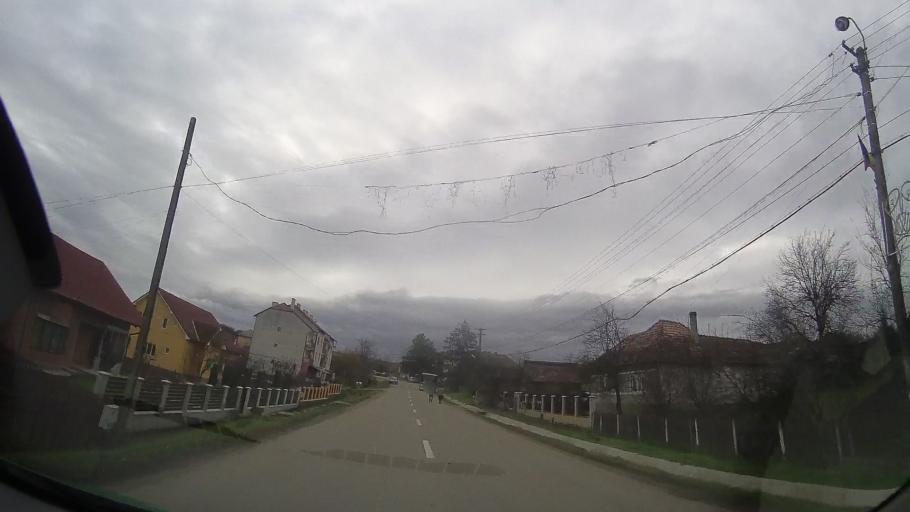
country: RO
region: Bistrita-Nasaud
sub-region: Comuna Milas
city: Milas
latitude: 46.8190
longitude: 24.4369
